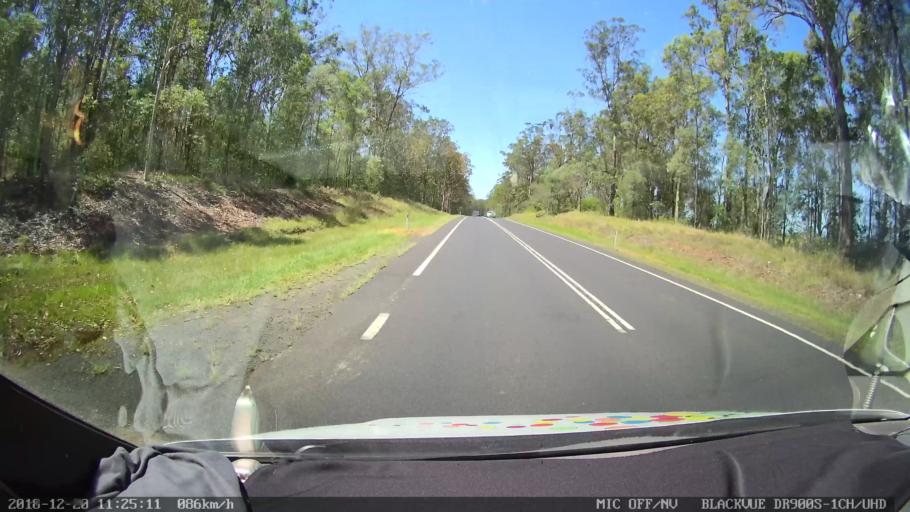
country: AU
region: New South Wales
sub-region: Richmond Valley
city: Casino
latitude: -29.0842
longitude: 153.0006
